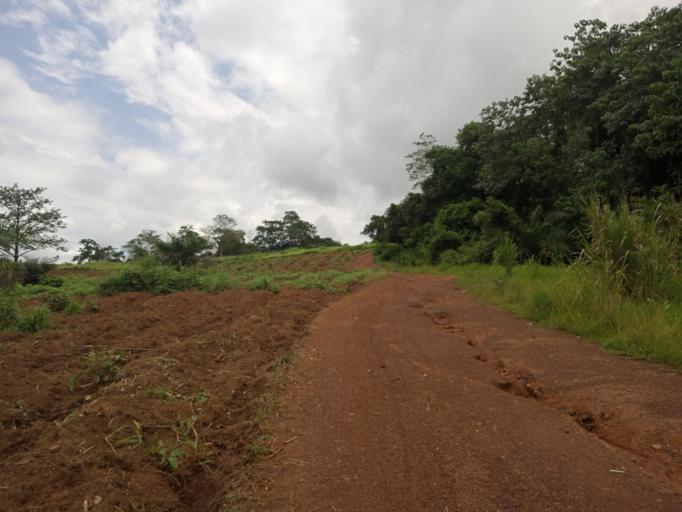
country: SL
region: Northern Province
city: Kamakwie
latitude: 9.4807
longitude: -12.2448
